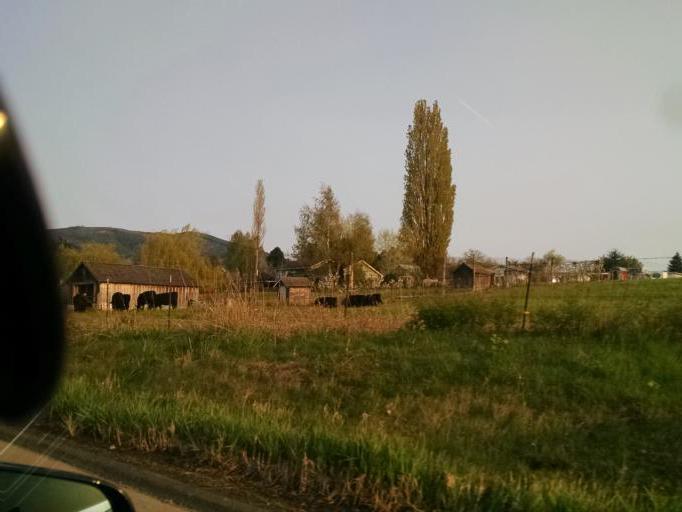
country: US
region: Washington
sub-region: Whatcom County
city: Geneva
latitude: 48.8037
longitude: -122.3567
